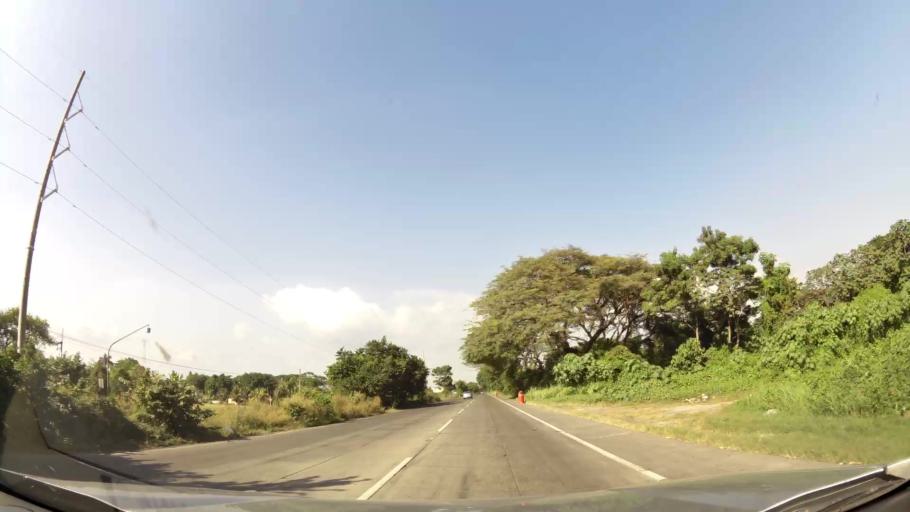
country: GT
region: Escuintla
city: Puerto San Jose
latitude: 13.9715
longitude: -90.7885
